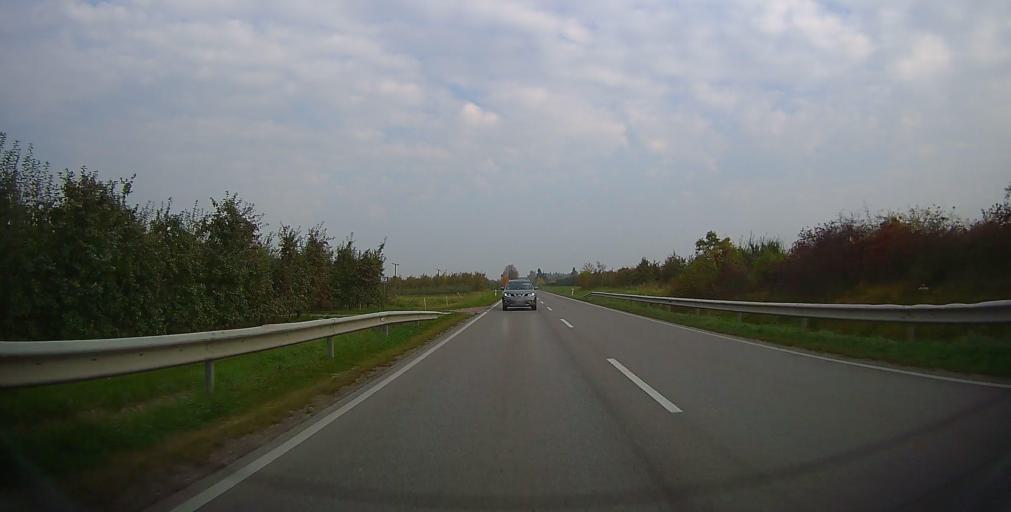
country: PL
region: Masovian Voivodeship
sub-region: Powiat grojecki
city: Belsk Duzy
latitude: 51.7806
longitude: 20.7740
